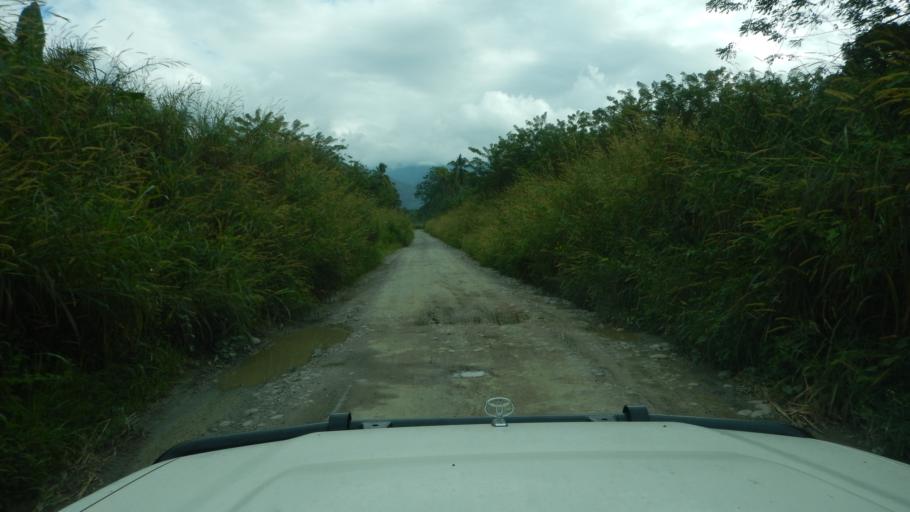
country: PG
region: Northern Province
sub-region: Sohe
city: Kokoda
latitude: -8.9113
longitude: 147.7938
